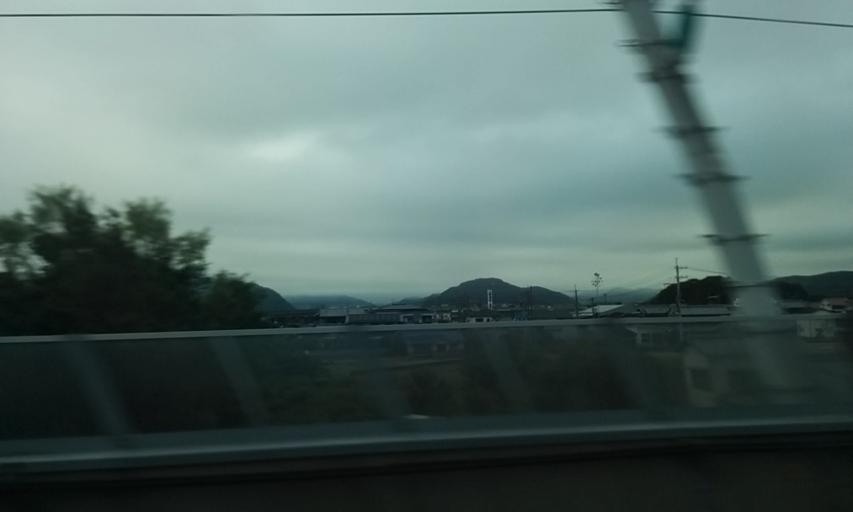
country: JP
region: Hyogo
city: Tatsunocho-tominaga
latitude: 34.8298
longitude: 134.5563
